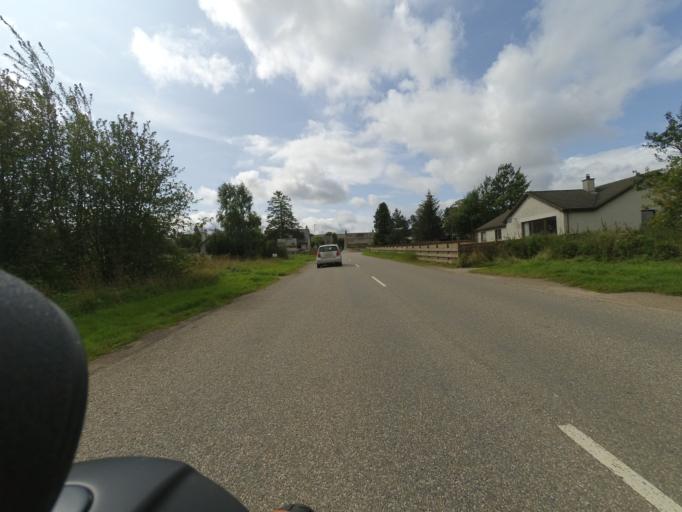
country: GB
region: Scotland
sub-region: Highland
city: Grantown on Spey
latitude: 57.2515
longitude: -3.3764
